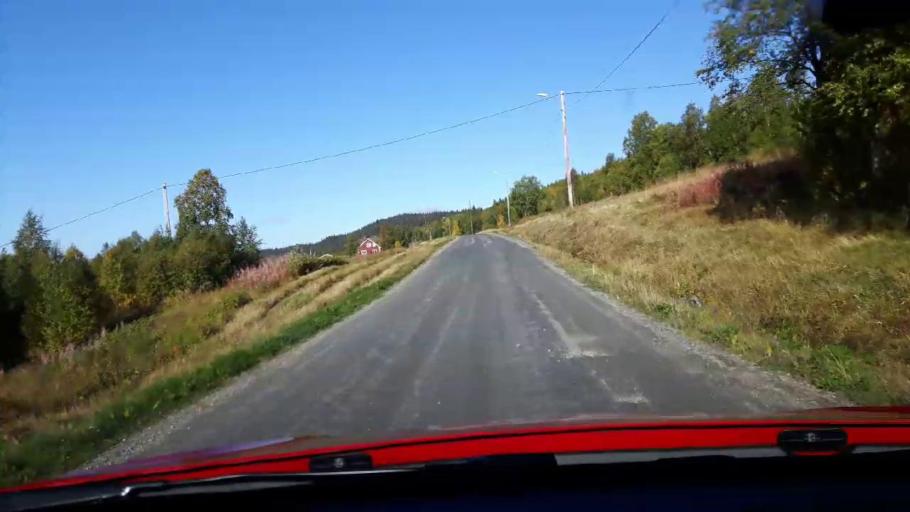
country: NO
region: Nord-Trondelag
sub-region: Lierne
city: Sandvika
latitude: 64.6065
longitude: 13.7787
